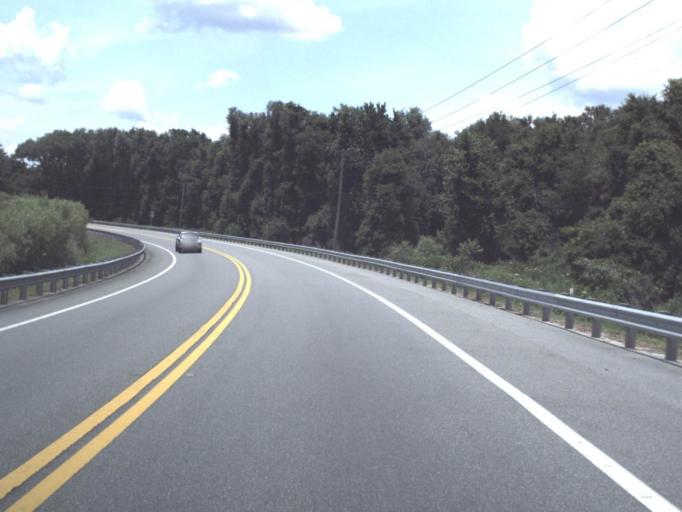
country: US
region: Florida
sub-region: Clay County
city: Keystone Heights
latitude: 29.7368
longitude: -81.9604
